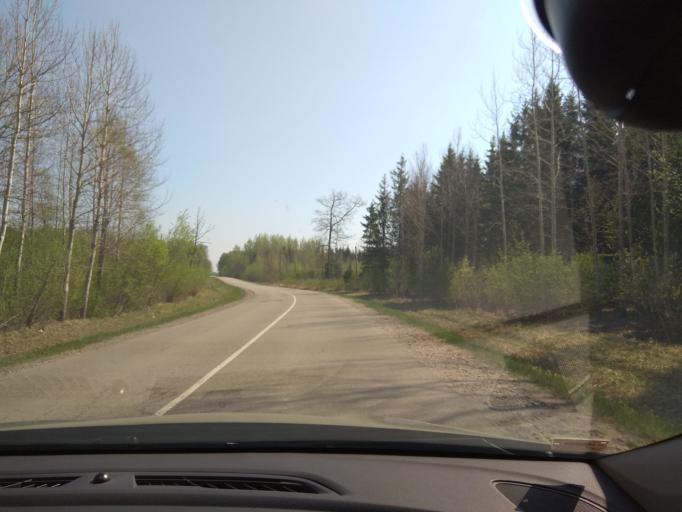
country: LT
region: Panevezys
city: Pasvalys
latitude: 55.9749
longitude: 24.1977
